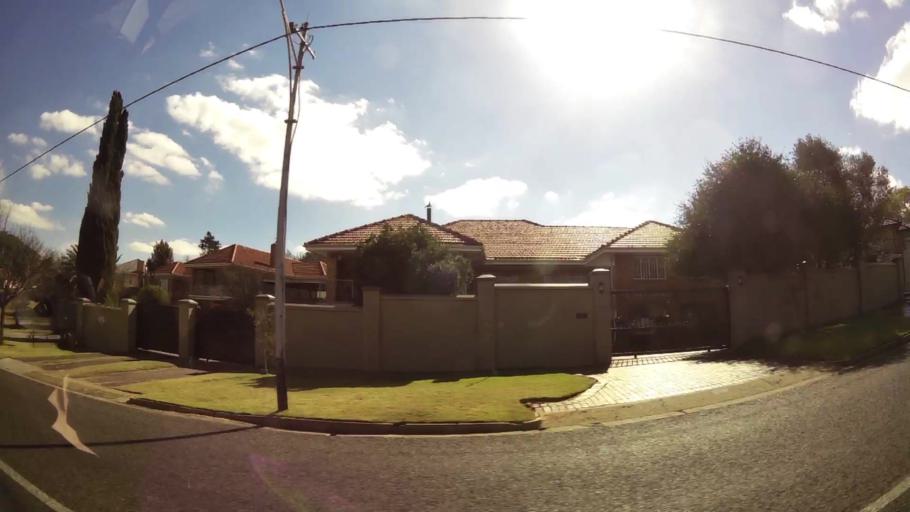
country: ZA
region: Gauteng
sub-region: West Rand District Municipality
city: Krugersdorp
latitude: -26.0963
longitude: 27.7845
